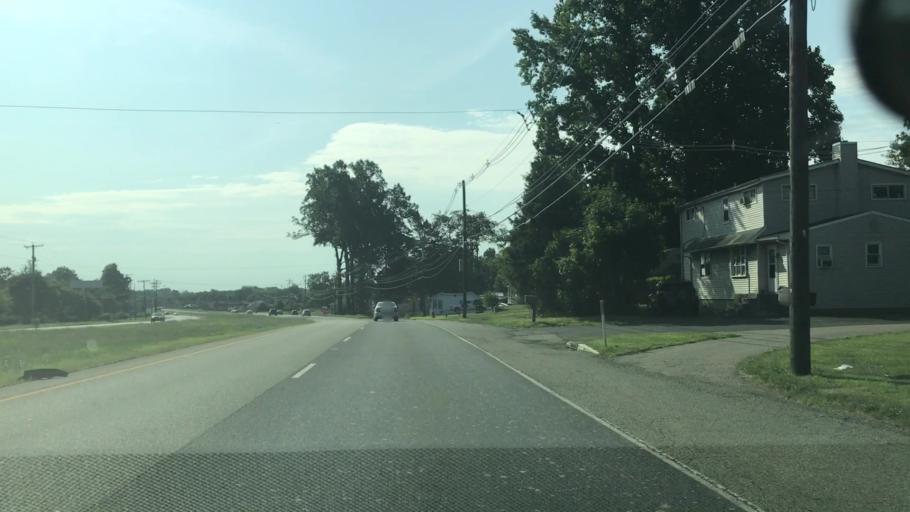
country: US
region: New Jersey
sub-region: Hunterdon County
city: Whitehouse Station
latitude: 40.6132
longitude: -74.7317
